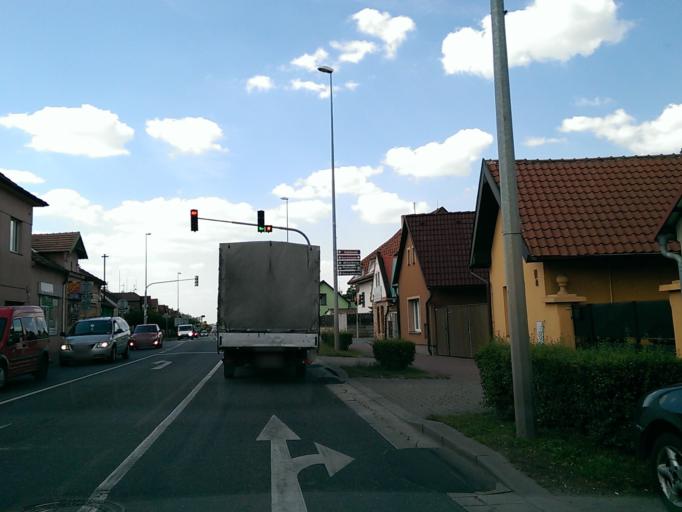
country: CZ
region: Praha
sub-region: Praha 14
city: Dolni Pocernice
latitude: 50.0587
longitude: 14.5598
